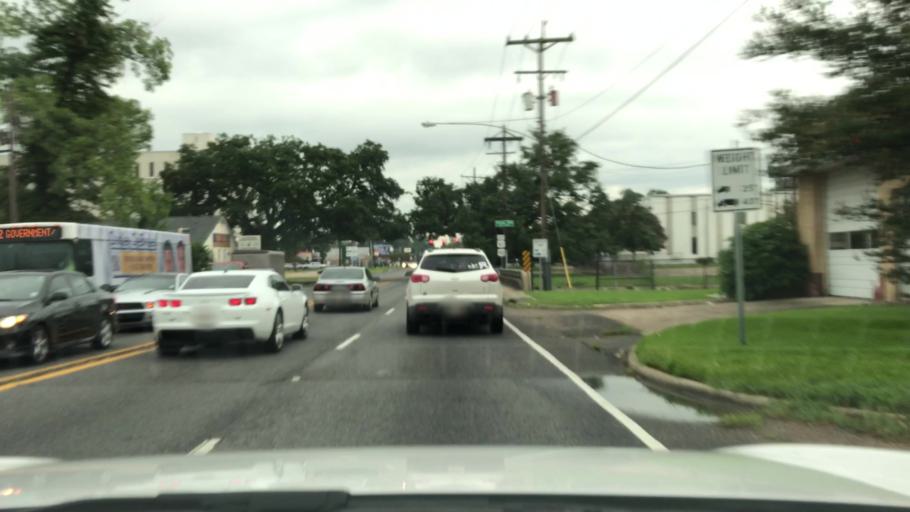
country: US
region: Louisiana
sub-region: East Baton Rouge Parish
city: Baton Rouge
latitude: 30.4489
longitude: -91.1389
